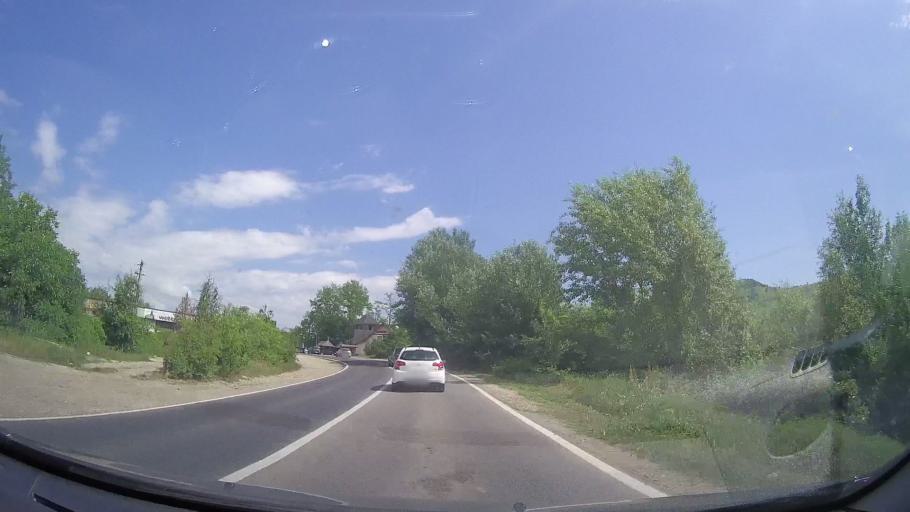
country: RO
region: Prahova
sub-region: Comuna Gura Vitioarei
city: Fagetu
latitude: 45.1346
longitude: 26.0309
